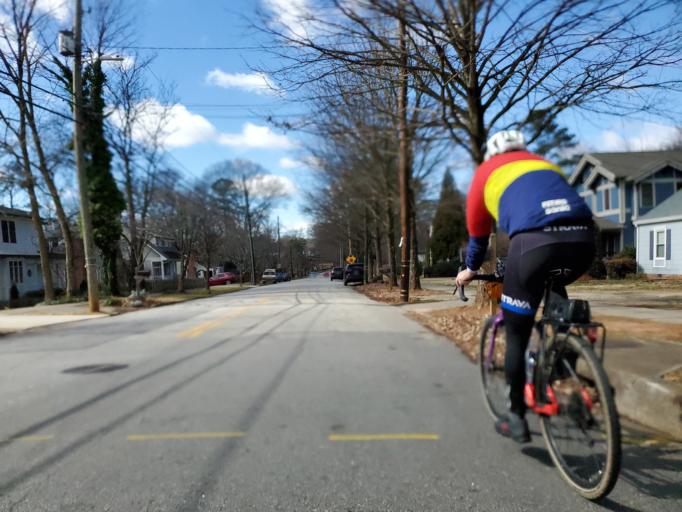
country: US
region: Georgia
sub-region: DeKalb County
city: Decatur
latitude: 33.7597
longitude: -84.3068
